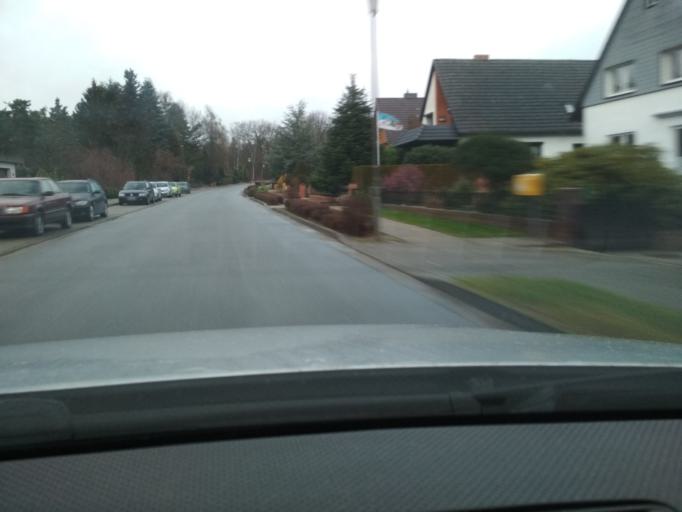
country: DE
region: Lower Saxony
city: Barwedel
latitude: 52.5177
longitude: 10.7745
